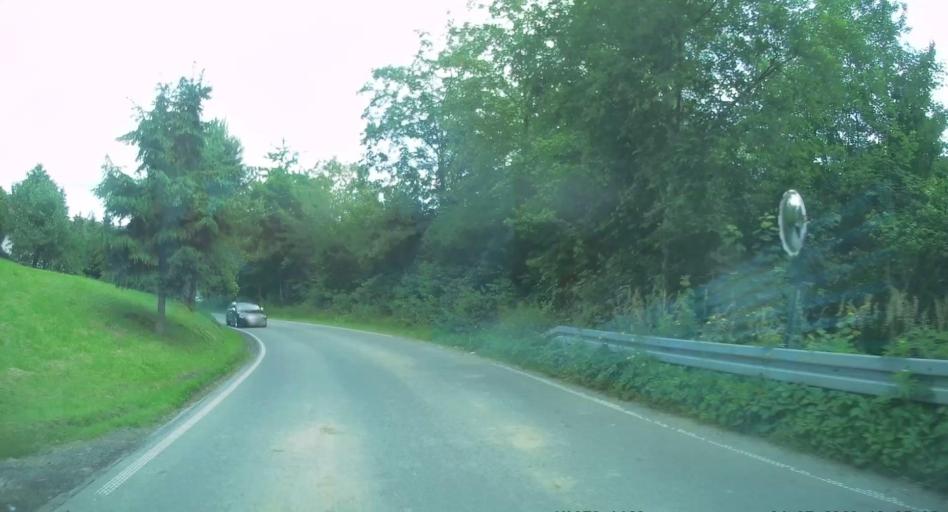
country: PL
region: Lesser Poland Voivodeship
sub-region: Powiat nowosadecki
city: Korzenna
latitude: 49.7165
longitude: 20.7761
